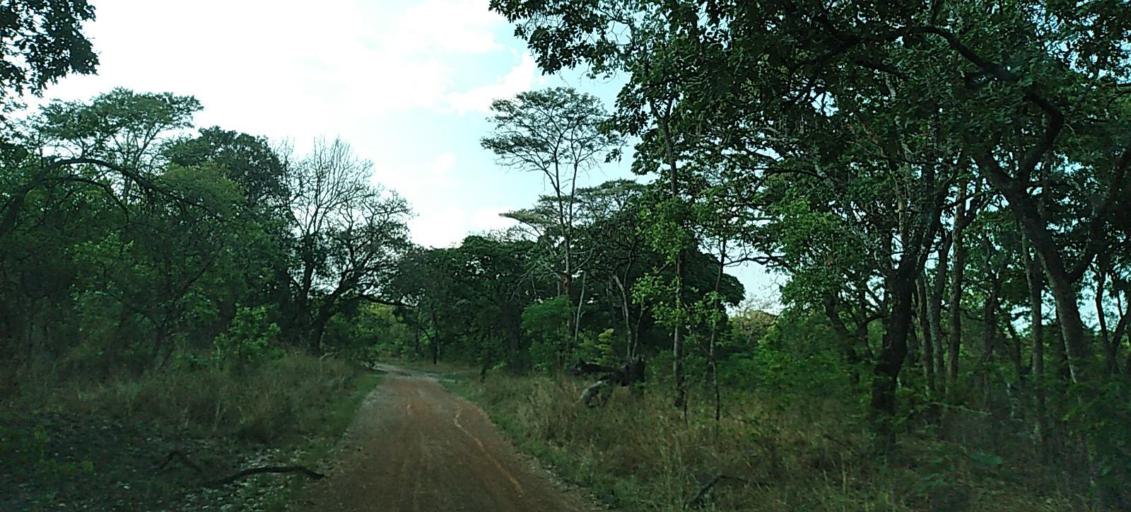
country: ZM
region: Copperbelt
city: Mpongwe
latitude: -13.4331
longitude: 28.0576
